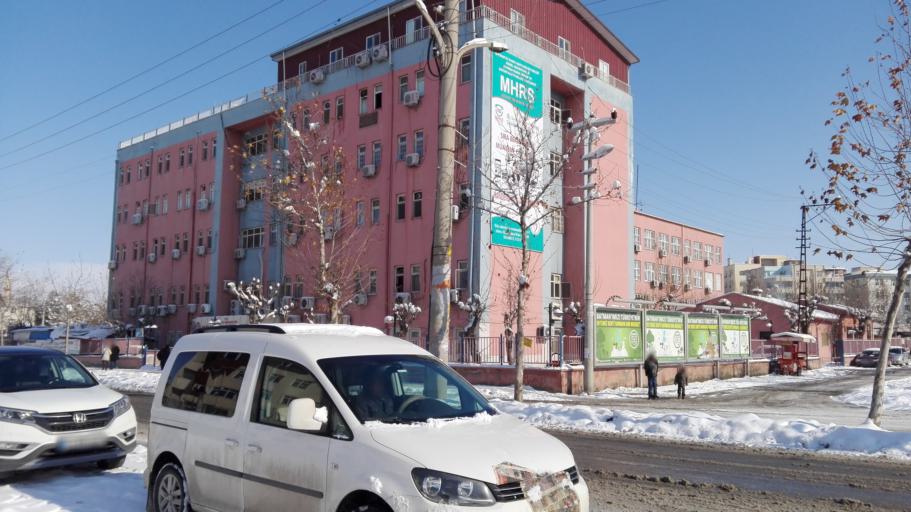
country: TR
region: Batman
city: Batman
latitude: 37.8890
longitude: 41.1250
